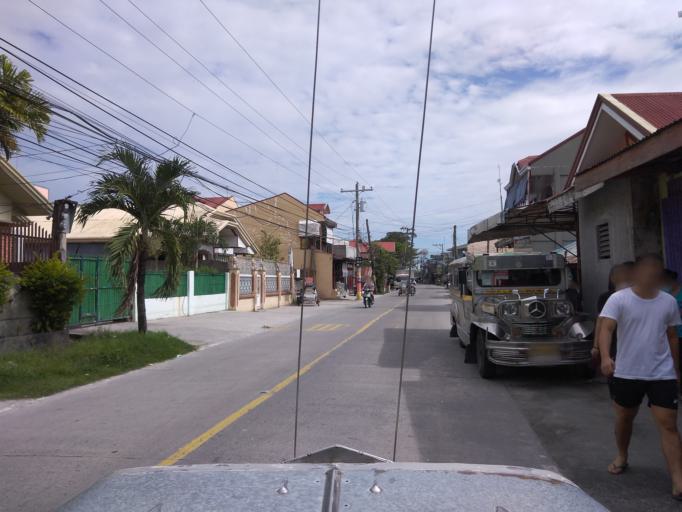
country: PH
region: Central Luzon
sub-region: Province of Pampanga
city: Sexmoan
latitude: 14.9509
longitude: 120.6251
